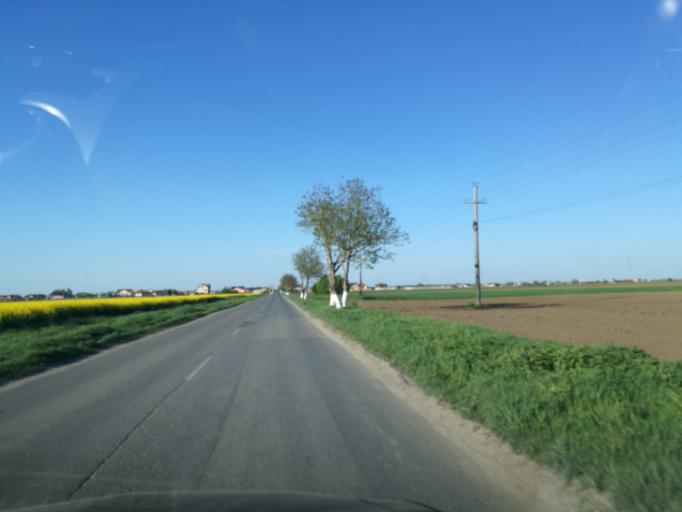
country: RO
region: Ilfov
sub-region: Comuna Vidra
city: Vidra
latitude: 44.2849
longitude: 26.1819
